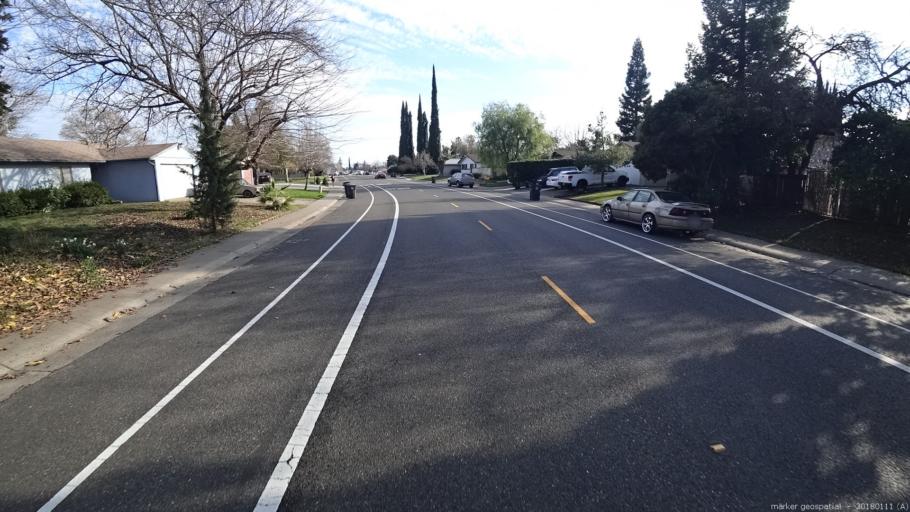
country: US
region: California
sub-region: Sacramento County
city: Rancho Cordova
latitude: 38.6127
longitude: -121.2935
